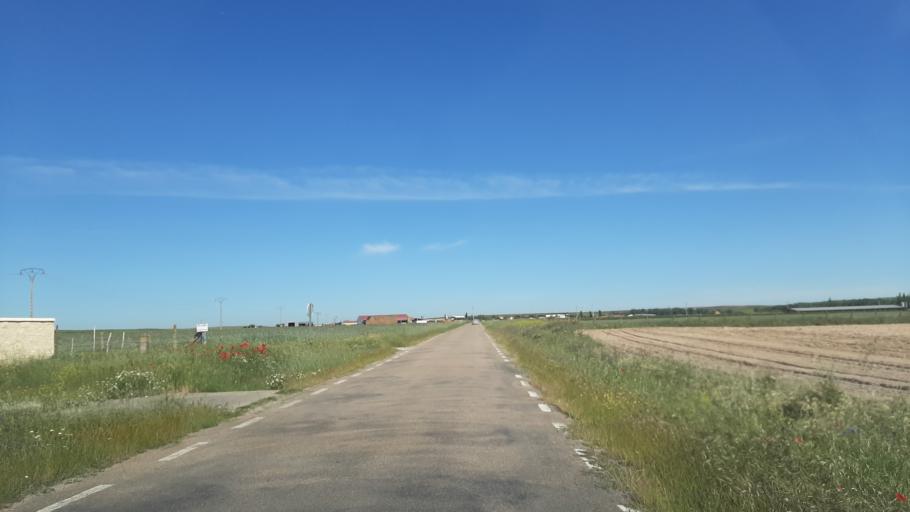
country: ES
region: Castille and Leon
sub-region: Provincia de Salamanca
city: Pedrosillo de Alba
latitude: 40.8139
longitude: -5.3870
